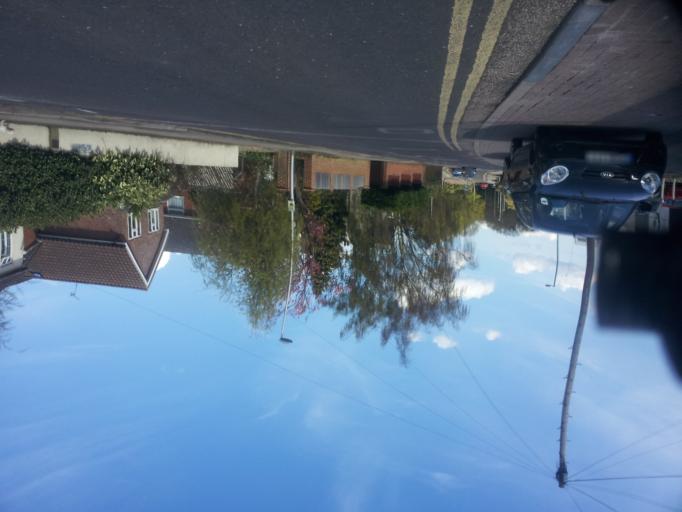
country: GB
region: England
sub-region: Kent
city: Rainham
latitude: 51.3531
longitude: 0.5805
